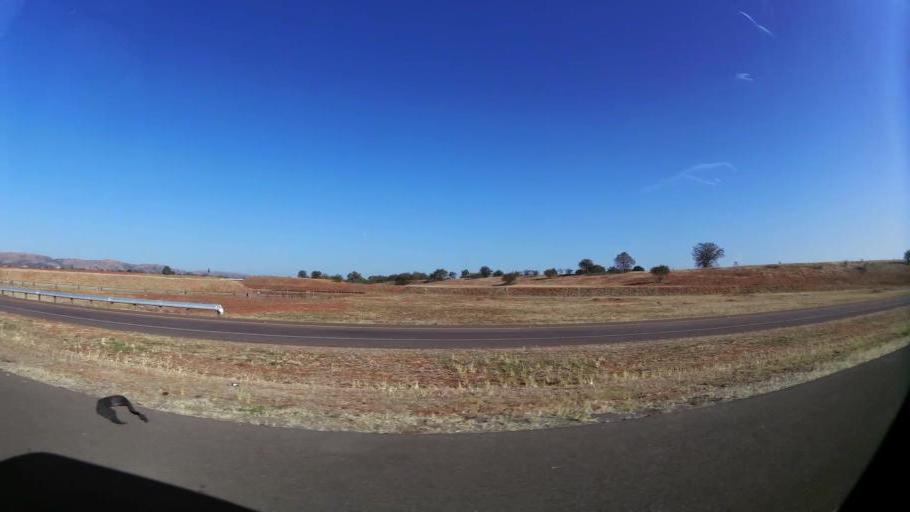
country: ZA
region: Gauteng
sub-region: City of Tshwane Metropolitan Municipality
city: Pretoria
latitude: -25.6525
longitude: 28.1132
